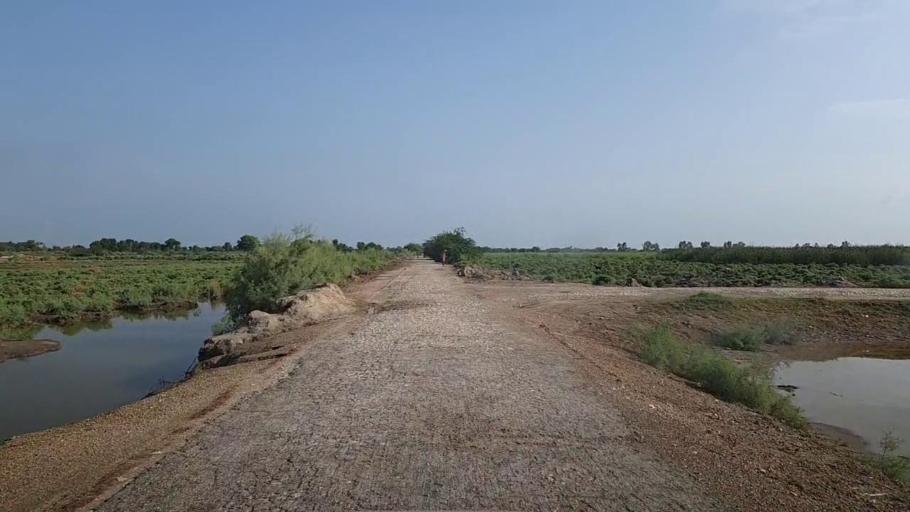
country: PK
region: Sindh
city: Pad Idan
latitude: 26.8222
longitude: 68.2381
